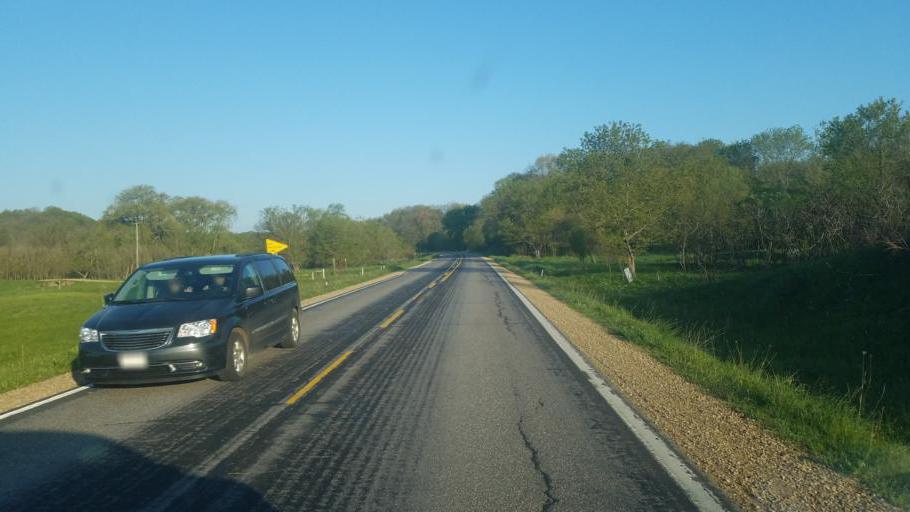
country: US
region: Wisconsin
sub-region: Vernon County
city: Hillsboro
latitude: 43.6446
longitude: -90.4169
